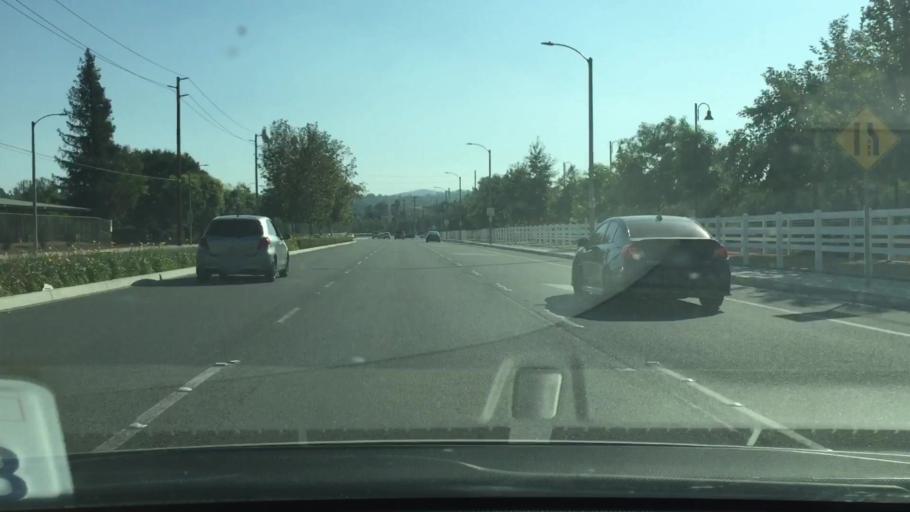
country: US
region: California
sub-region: San Bernardino County
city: Chino Hills
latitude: 33.9923
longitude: -117.7327
